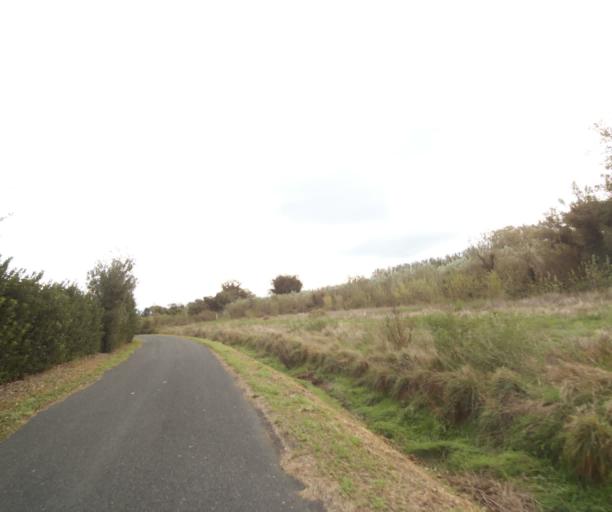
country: FR
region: Languedoc-Roussillon
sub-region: Departement des Pyrenees-Orientales
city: Argelers
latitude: 42.5780
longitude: 3.0263
